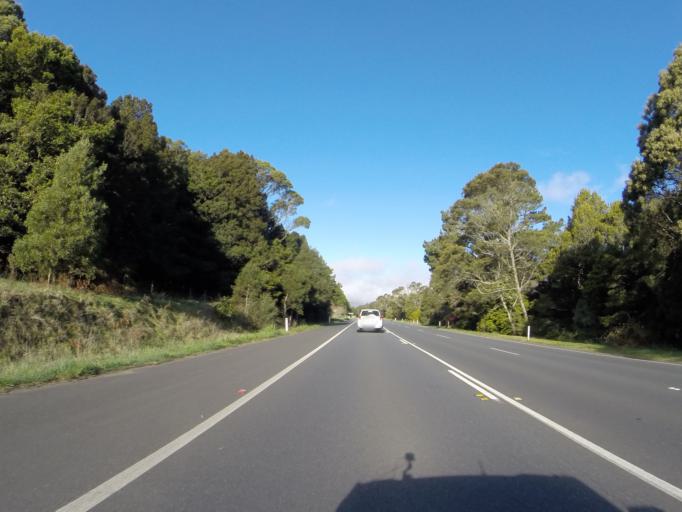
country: AU
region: New South Wales
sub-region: Shellharbour
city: Calderwood
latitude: -34.5893
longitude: 150.5664
